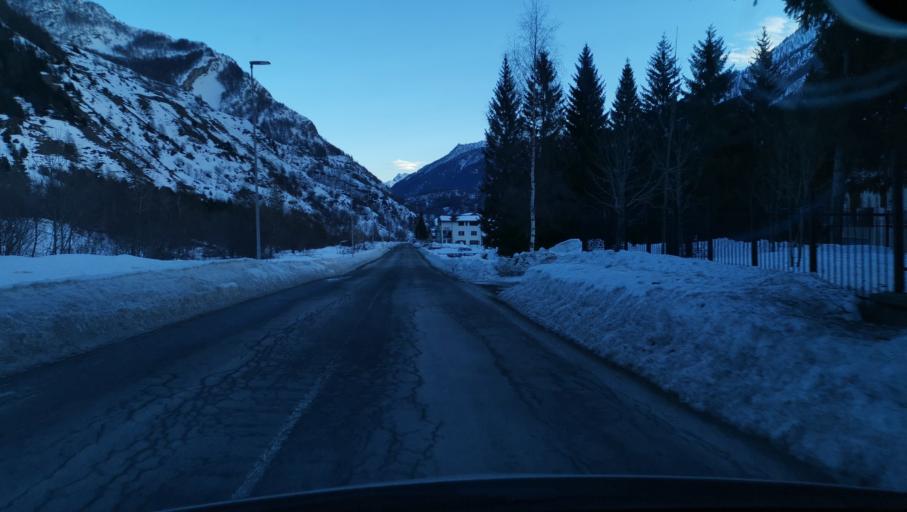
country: IT
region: Piedmont
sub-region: Provincia di Cuneo
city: Bersezio
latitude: 44.3700
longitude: 6.9815
